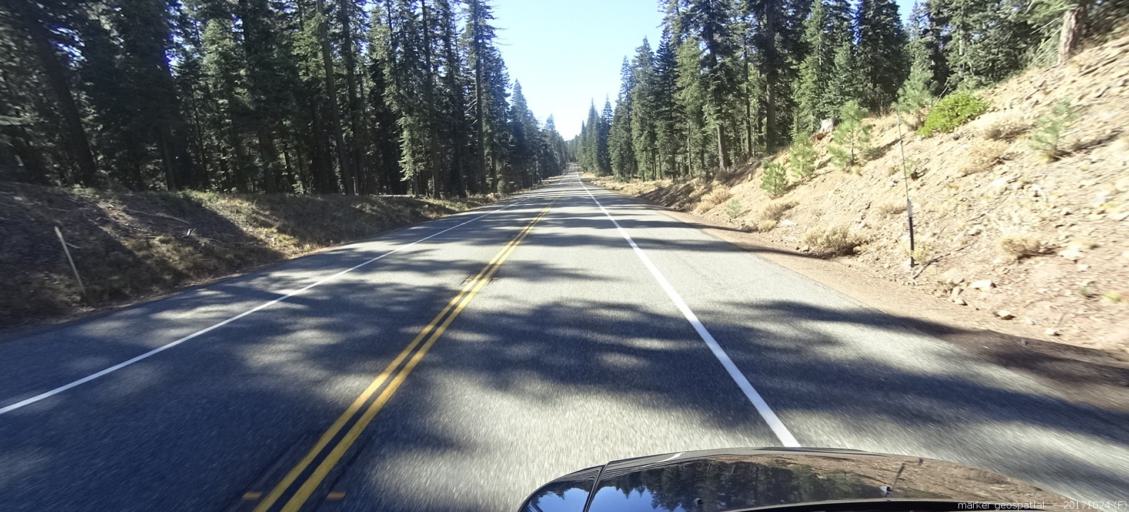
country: US
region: California
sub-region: Shasta County
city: Burney
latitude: 40.5914
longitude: -121.5388
